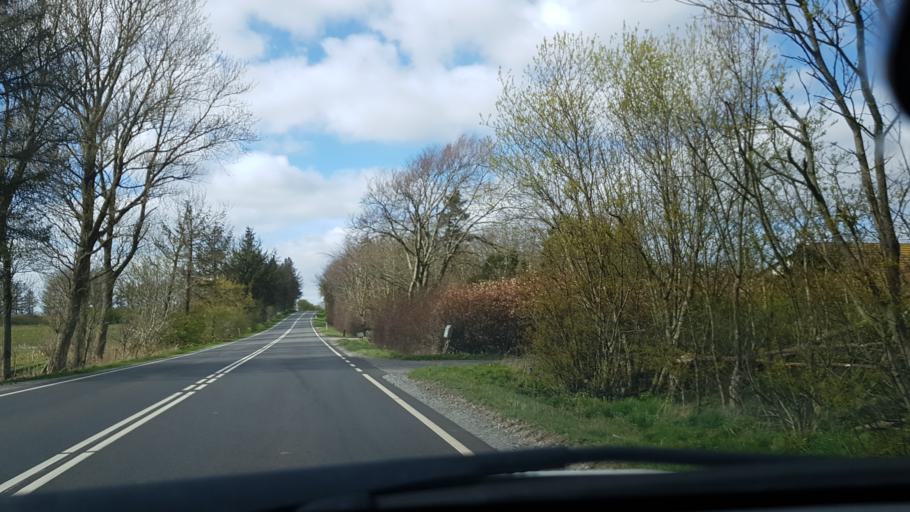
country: DK
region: South Denmark
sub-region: Esbjerg Kommune
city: Ribe
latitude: 55.2706
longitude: 8.8727
